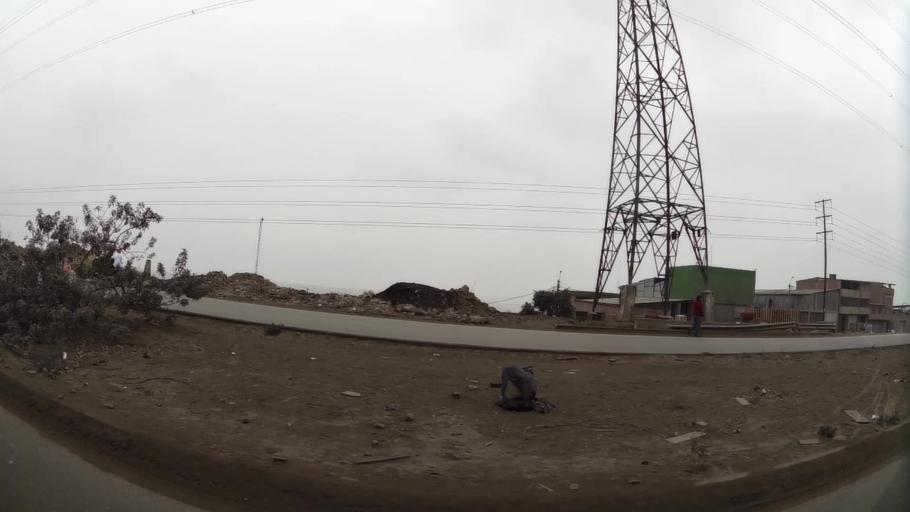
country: PE
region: Lima
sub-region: Lima
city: Surco
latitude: -12.2105
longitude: -76.9263
